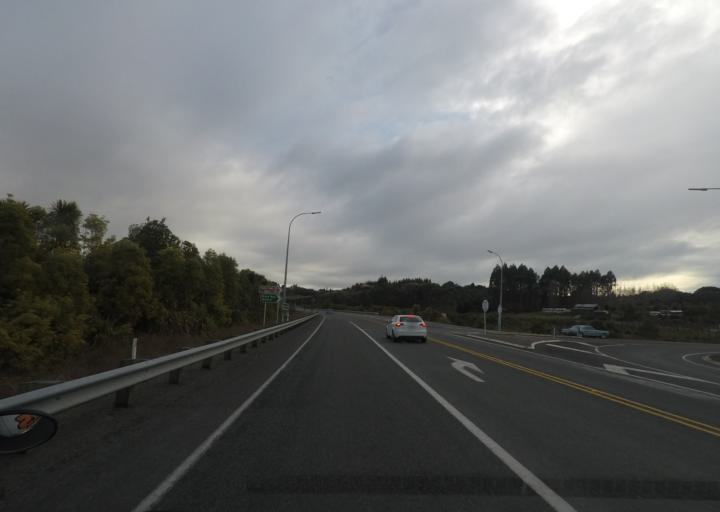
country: NZ
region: Tasman
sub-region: Tasman District
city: Mapua
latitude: -41.2532
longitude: 173.0710
